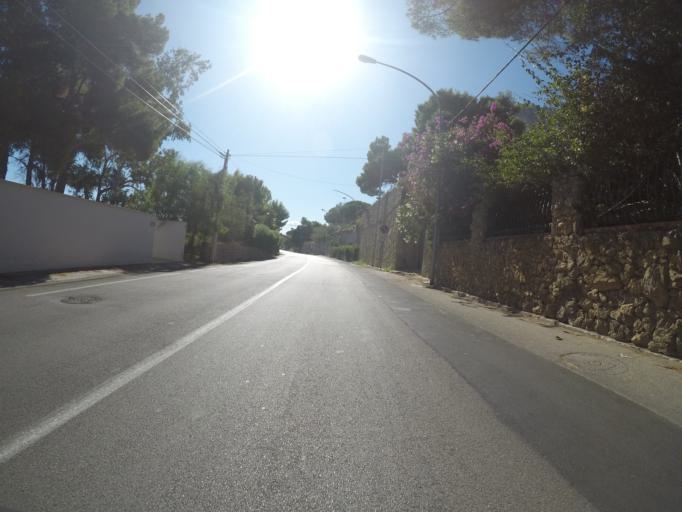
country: IT
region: Sicily
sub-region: Palermo
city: Palermo
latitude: 38.1874
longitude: 13.3602
